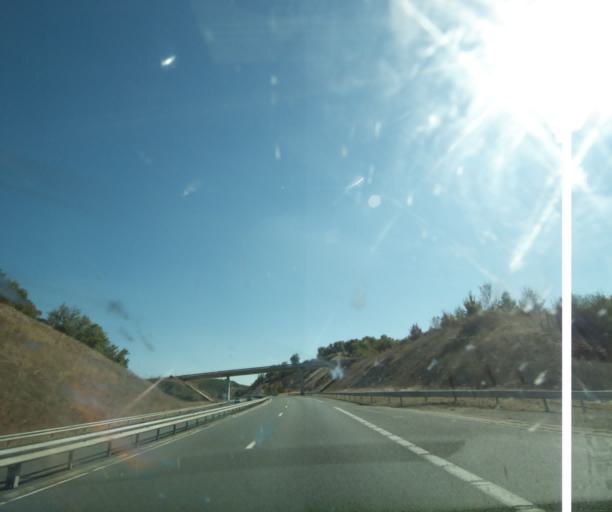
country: FR
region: Midi-Pyrenees
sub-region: Departement du Lot
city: Souillac
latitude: 44.8435
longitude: 1.4913
